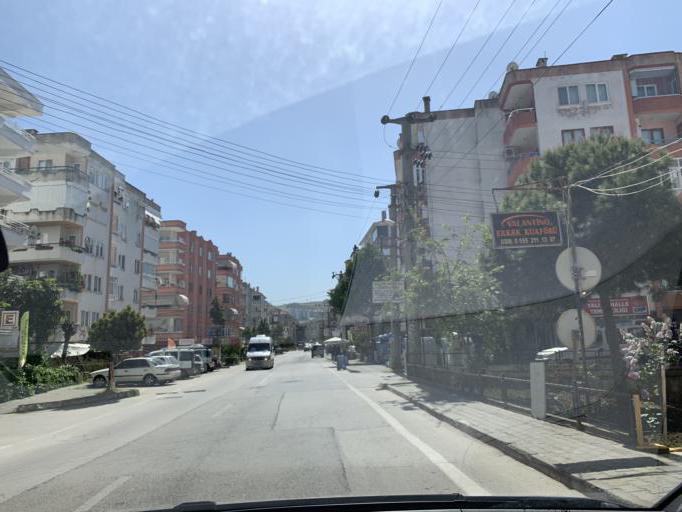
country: TR
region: Bursa
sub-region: Mudanya
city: Mudanya
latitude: 40.3562
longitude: 28.9208
